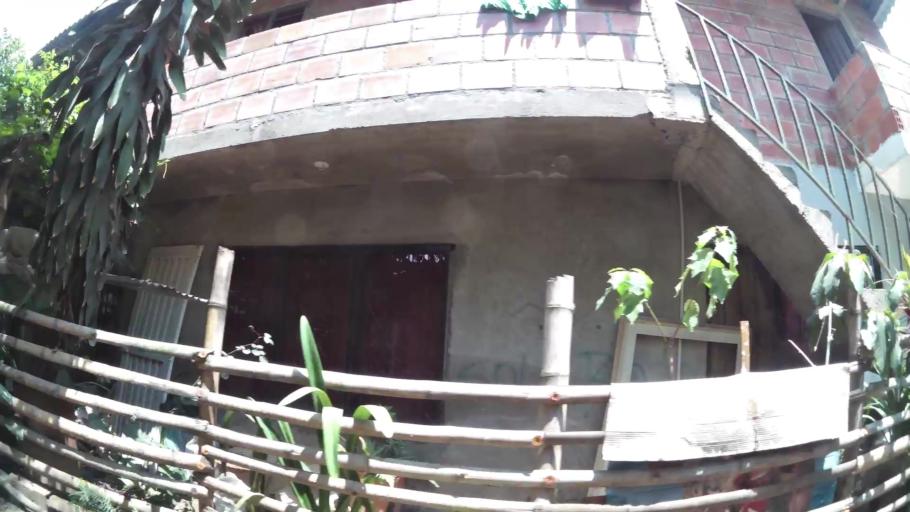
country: CO
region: Valle del Cauca
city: Cali
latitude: 3.4560
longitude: -76.4758
